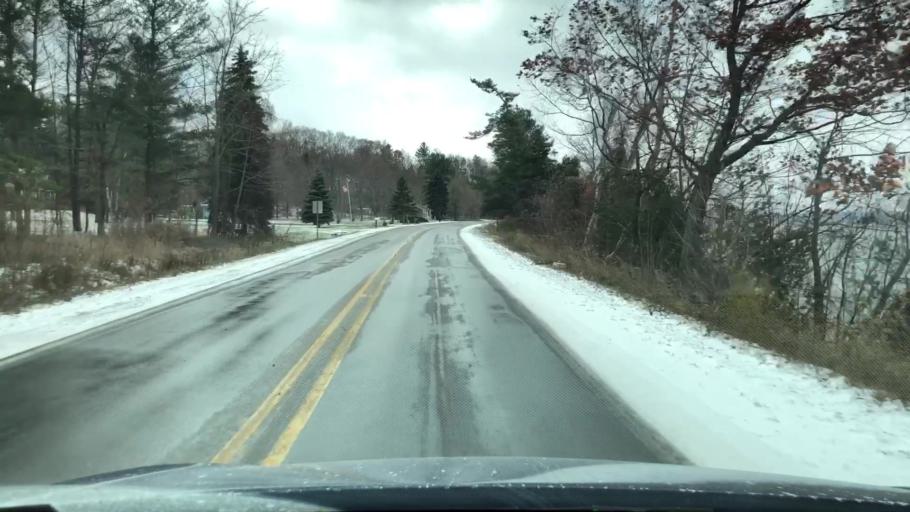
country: US
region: Michigan
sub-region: Leelanau County
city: Greilickville
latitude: 44.8439
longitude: -85.5578
